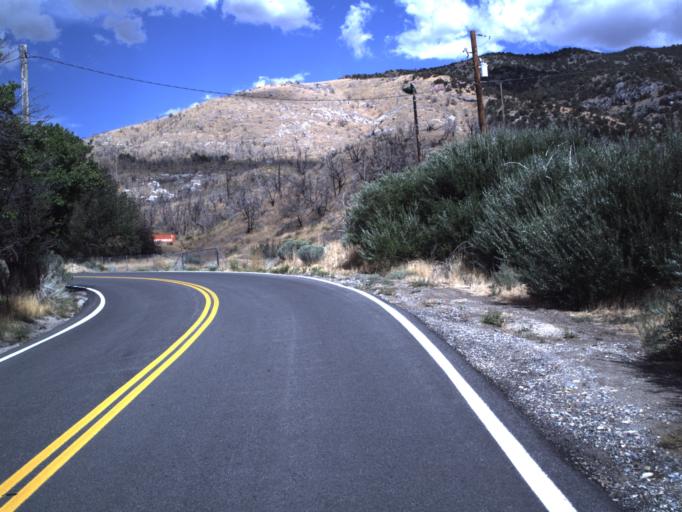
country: US
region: Utah
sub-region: Tooele County
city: Grantsville
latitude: 40.3380
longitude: -112.6111
